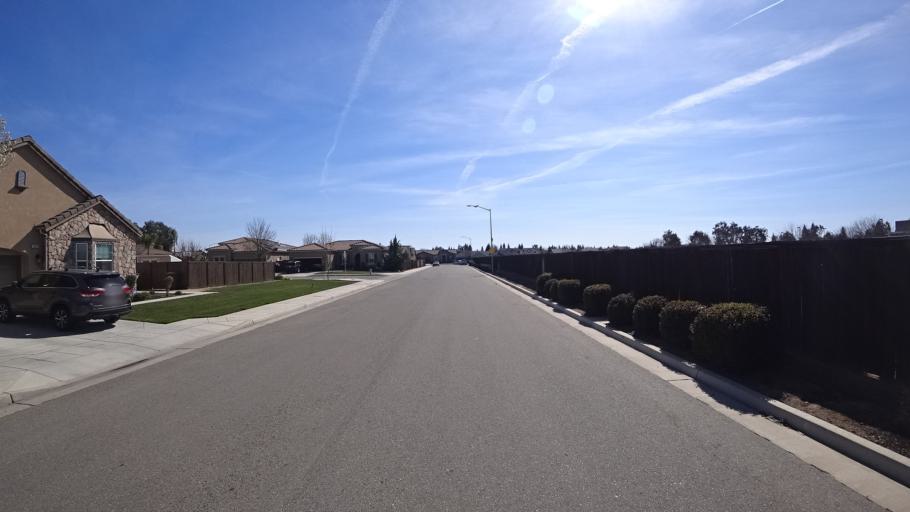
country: US
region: California
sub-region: Fresno County
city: Clovis
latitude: 36.8508
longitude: -119.7327
